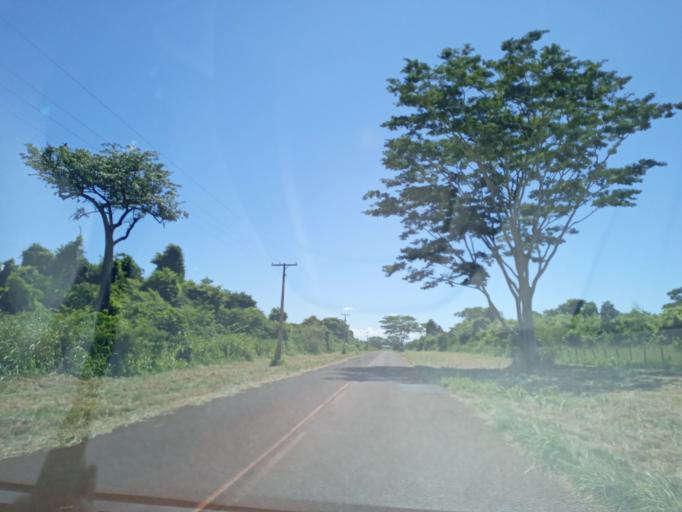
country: BR
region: Goias
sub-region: Itumbiara
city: Itumbiara
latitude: -18.4165
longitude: -49.1335
